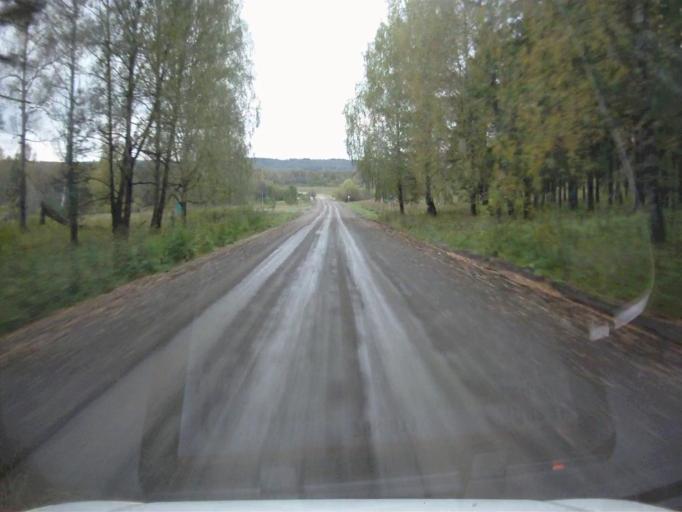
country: RU
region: Chelyabinsk
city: Nyazepetrovsk
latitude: 56.1232
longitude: 59.3583
